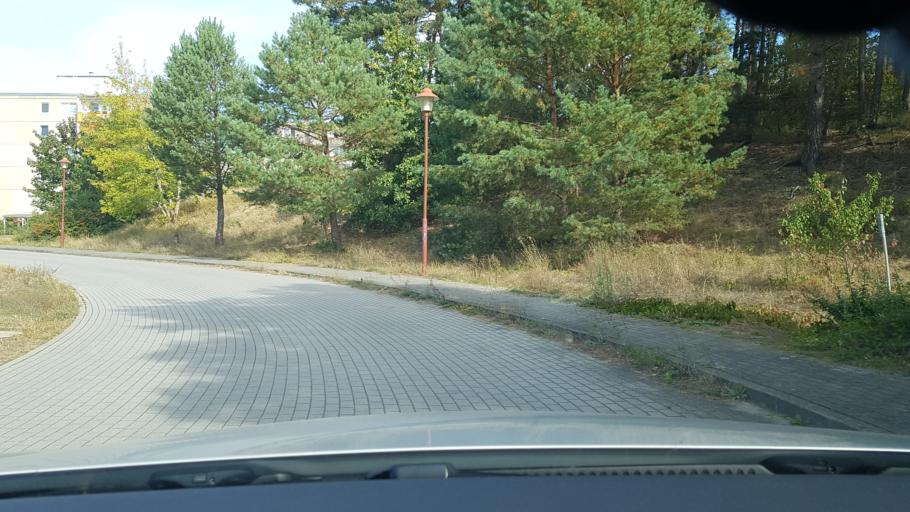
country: DE
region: Brandenburg
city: Lawitz
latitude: 52.1279
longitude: 14.6418
